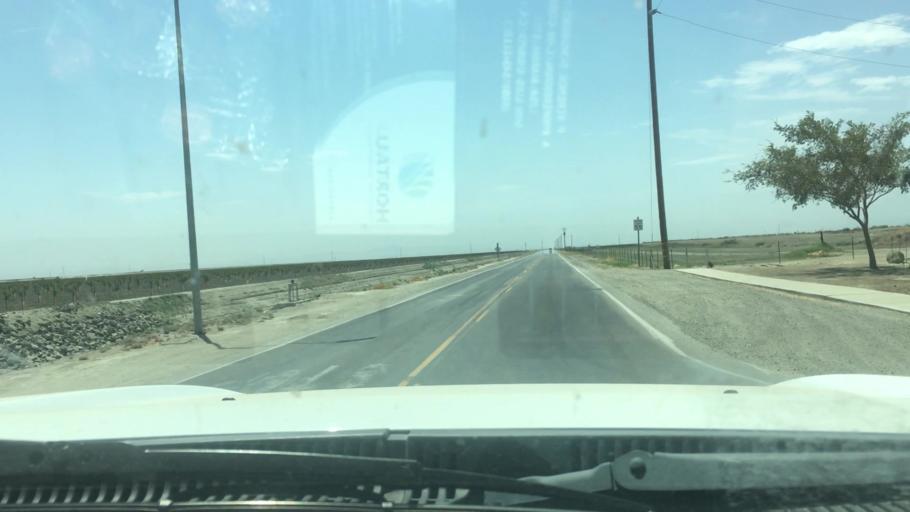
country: US
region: California
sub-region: Kings County
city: Corcoran
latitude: 36.0508
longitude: -119.5579
